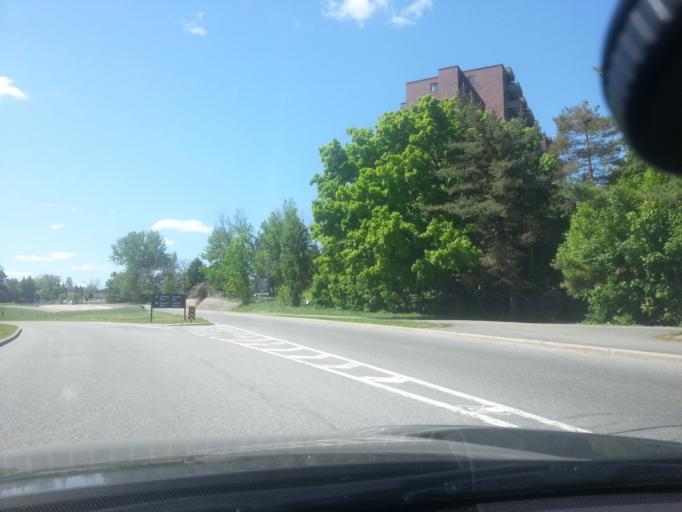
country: CA
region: Ontario
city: Bells Corners
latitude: 45.3670
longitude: -75.7837
